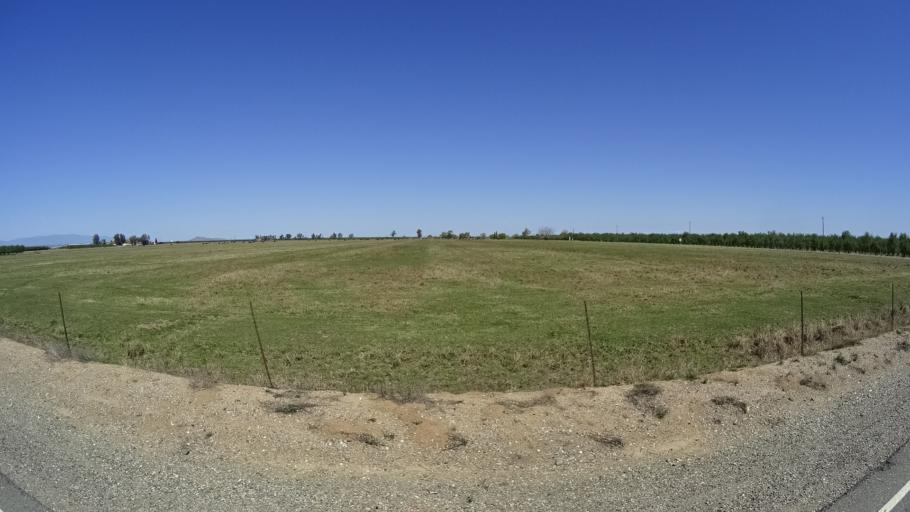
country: US
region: California
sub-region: Glenn County
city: Willows
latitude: 39.6244
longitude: -122.2360
